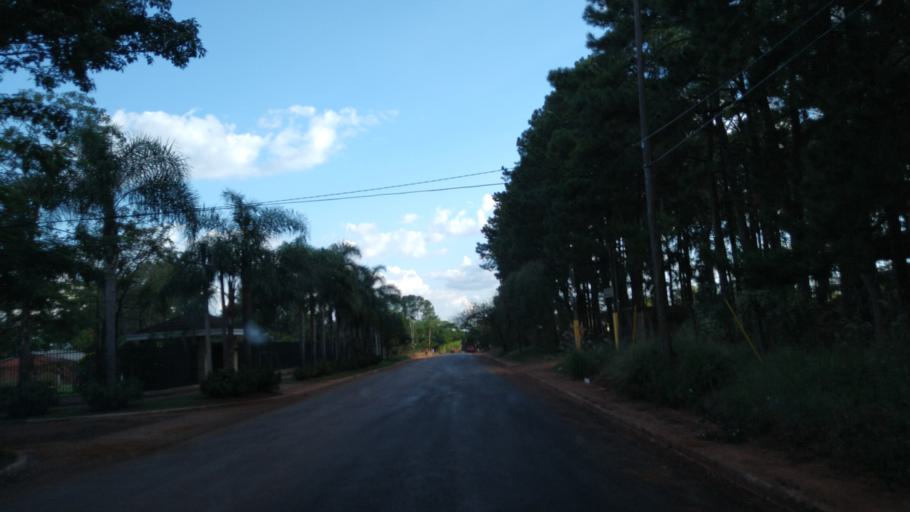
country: AR
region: Misiones
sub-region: Departamento de Capital
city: Posadas
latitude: -27.4041
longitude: -55.9284
